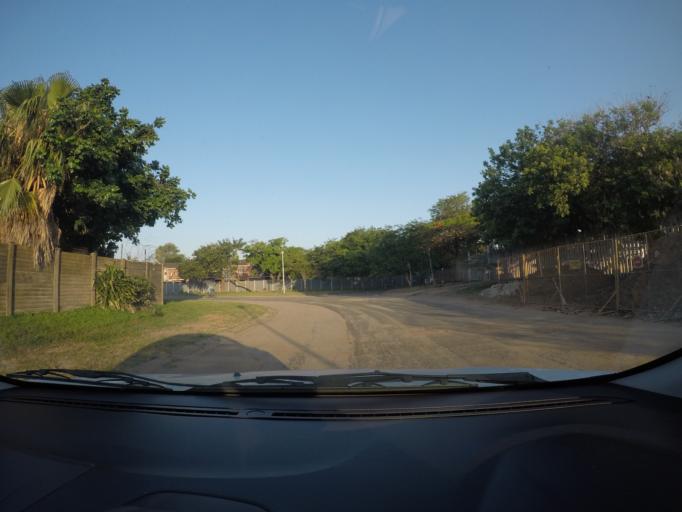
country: ZA
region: KwaZulu-Natal
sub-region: uThungulu District Municipality
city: Richards Bay
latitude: -28.7812
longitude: 32.1015
